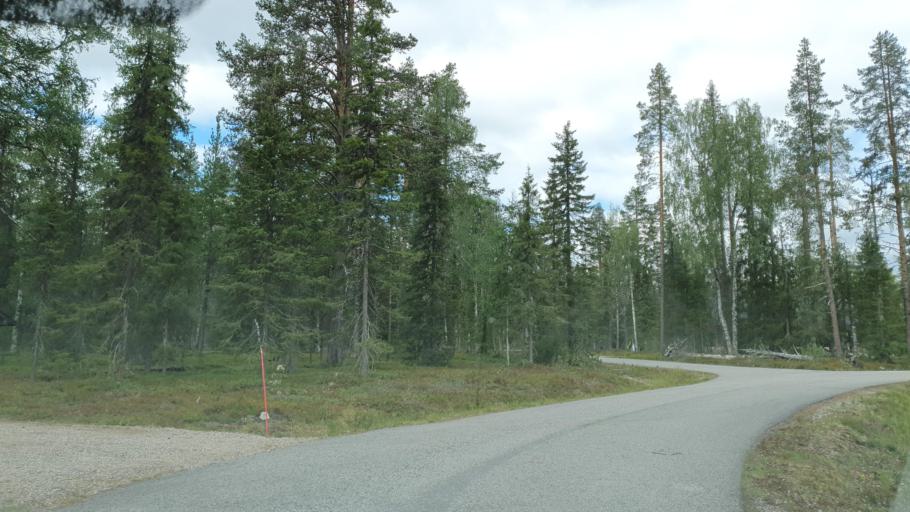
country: FI
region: Lapland
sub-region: Tunturi-Lappi
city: Kolari
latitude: 67.5503
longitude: 24.2772
